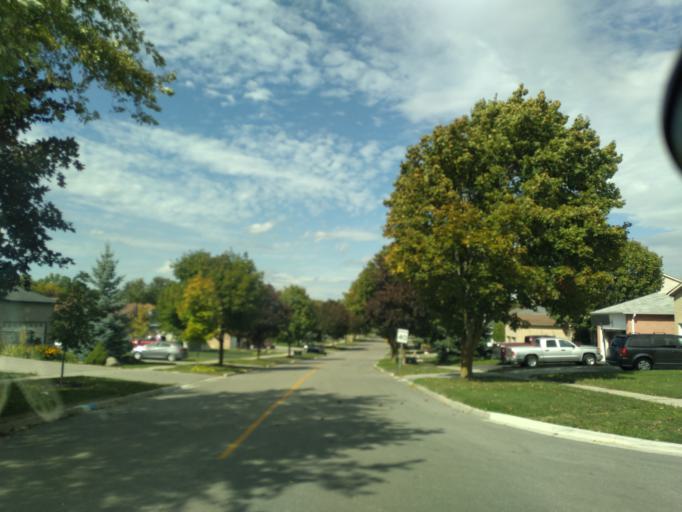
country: CA
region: Ontario
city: Newmarket
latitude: 44.0975
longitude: -79.4824
